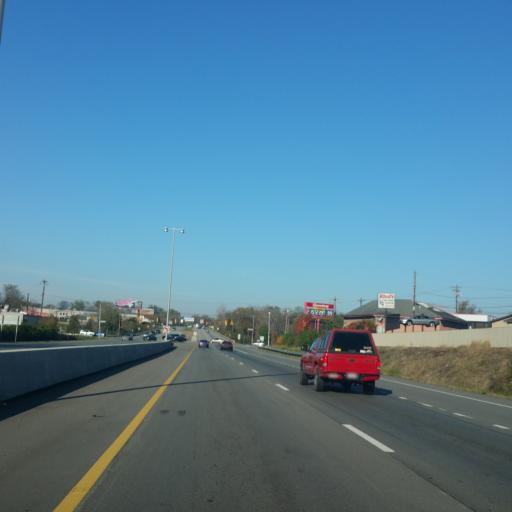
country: US
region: Ohio
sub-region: Clermont County
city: Summerside
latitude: 39.1035
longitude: -84.2897
